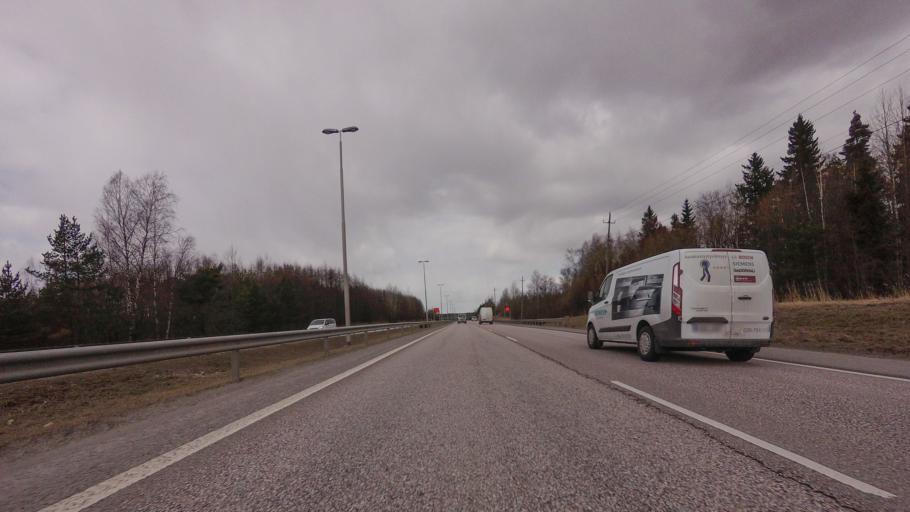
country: FI
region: Uusimaa
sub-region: Helsinki
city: Kilo
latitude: 60.3334
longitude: 24.8203
